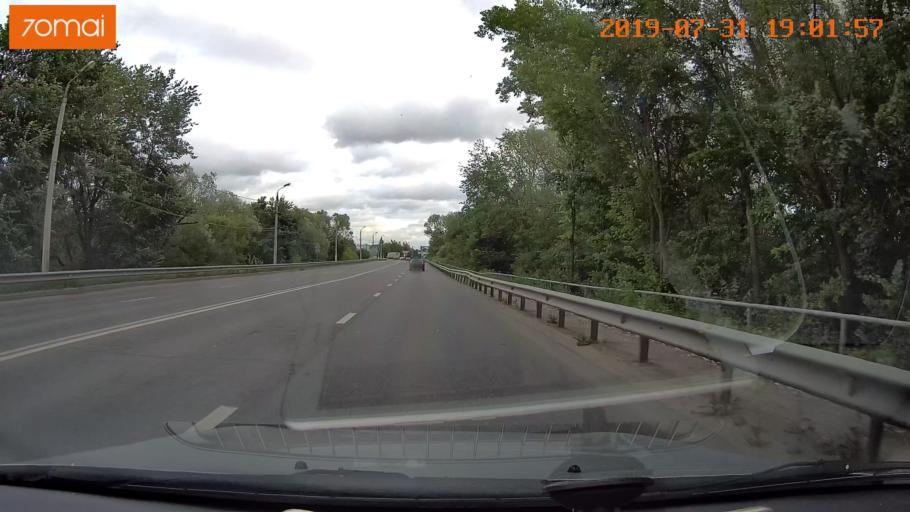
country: RU
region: Moskovskaya
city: Raduzhnyy
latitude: 55.1229
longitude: 38.7299
